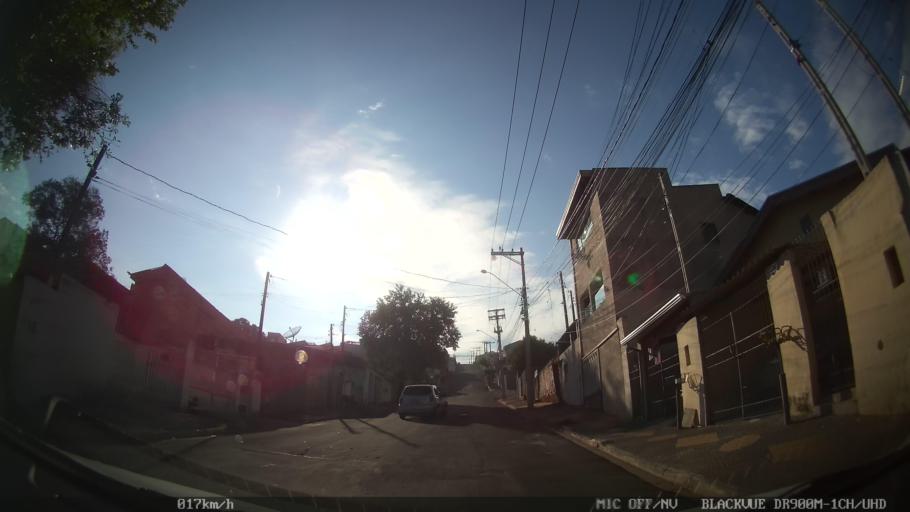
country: BR
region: Sao Paulo
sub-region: Americana
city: Americana
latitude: -22.7264
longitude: -47.3754
